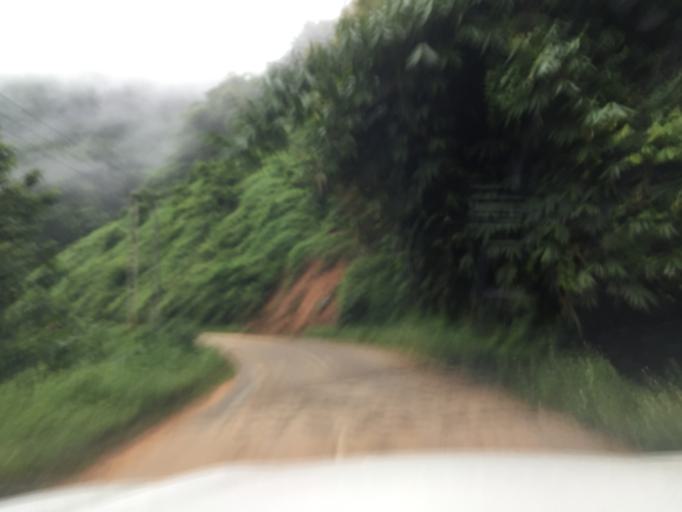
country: LA
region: Phongsali
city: Khoa
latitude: 21.0752
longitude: 102.3773
